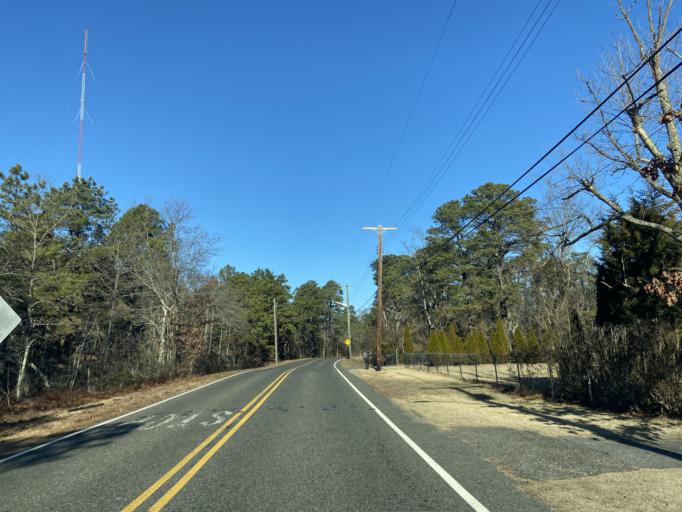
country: US
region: New Jersey
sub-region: Cumberland County
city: Vineland
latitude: 39.4966
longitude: -75.0735
